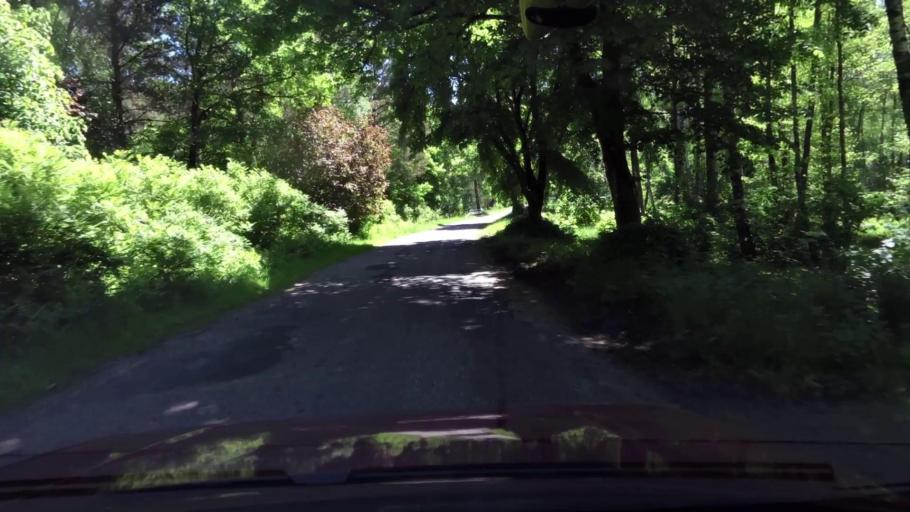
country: PL
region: West Pomeranian Voivodeship
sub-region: Powiat koszalinski
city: Bobolice
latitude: 54.0502
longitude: 16.5863
